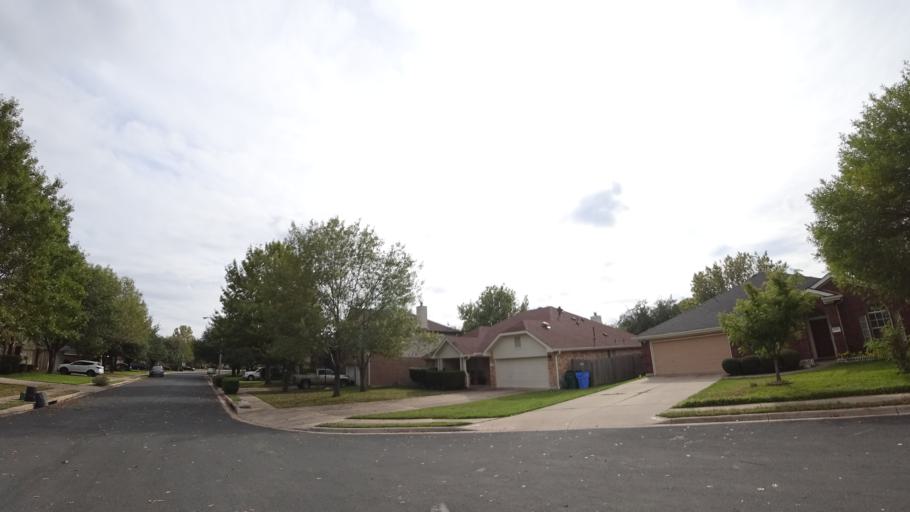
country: US
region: Texas
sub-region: Travis County
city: Wells Branch
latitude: 30.4451
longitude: -97.6751
